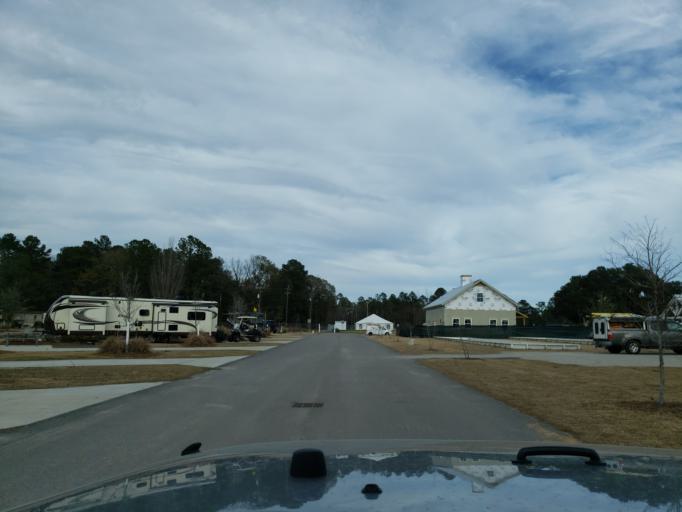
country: US
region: Georgia
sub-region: Bryan County
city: Richmond Hill
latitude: 32.0106
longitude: -81.2986
